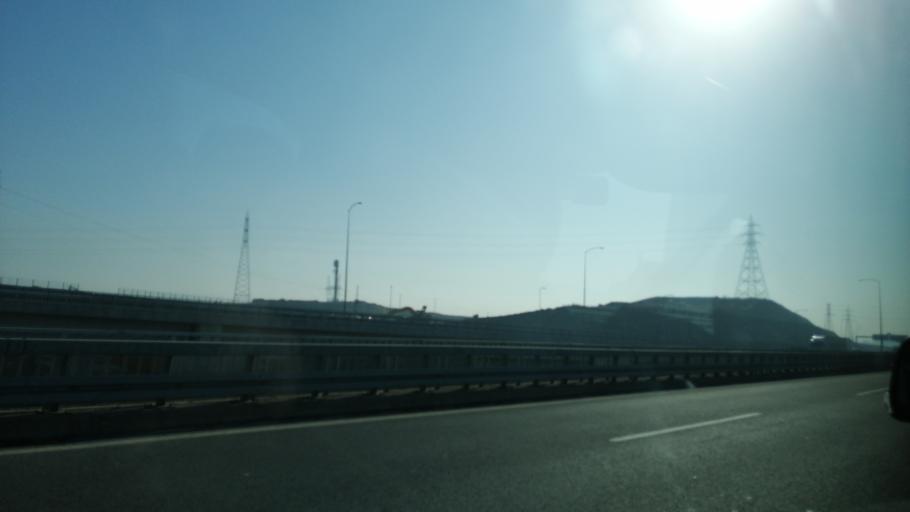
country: TR
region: Kocaeli
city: Tavsanli
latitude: 40.7959
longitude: 29.5097
